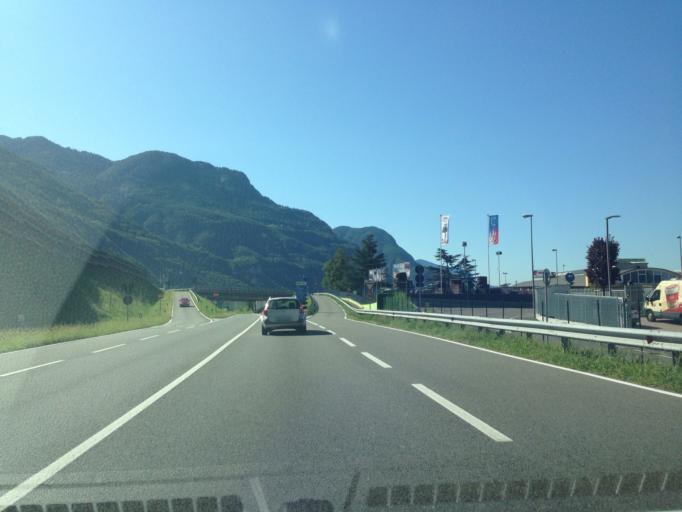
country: IT
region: Trentino-Alto Adige
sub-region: Bolzano
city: Pineta
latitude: 46.4449
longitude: 11.3432
